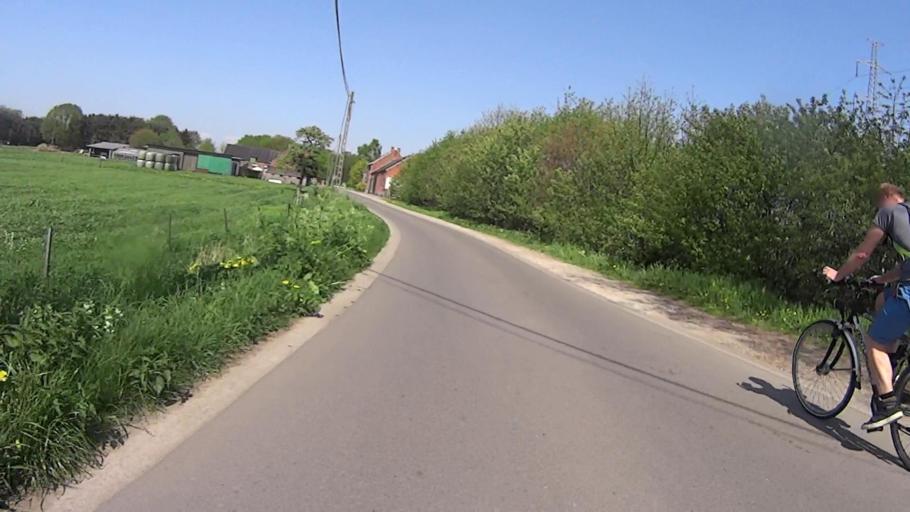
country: BE
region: Flanders
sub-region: Provincie Antwerpen
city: Sint-Amands
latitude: 51.0718
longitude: 4.2163
